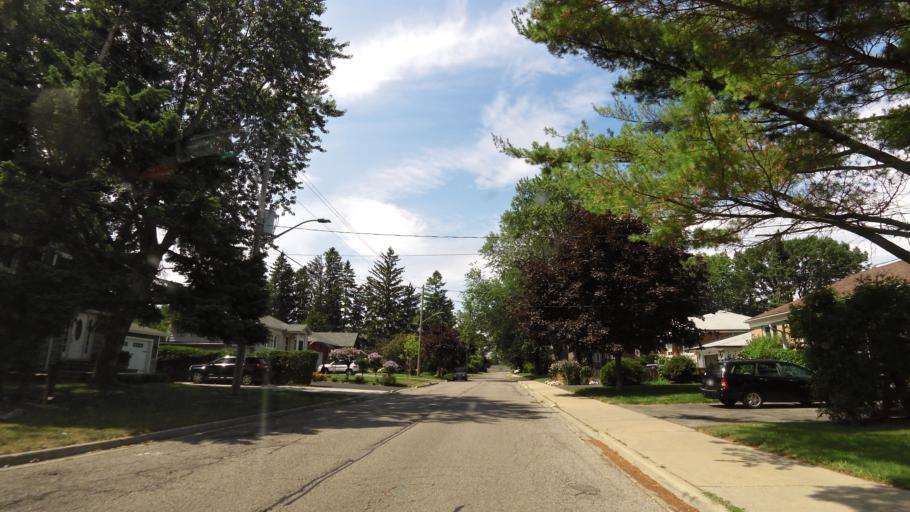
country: CA
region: Ontario
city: Mississauga
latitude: 43.5757
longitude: -79.5868
